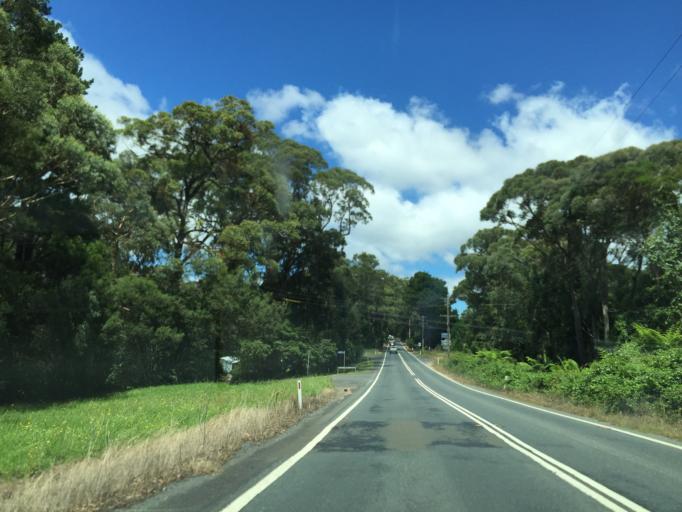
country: AU
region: New South Wales
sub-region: Blue Mountains Municipality
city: Lawson
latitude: -33.5224
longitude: 150.4608
